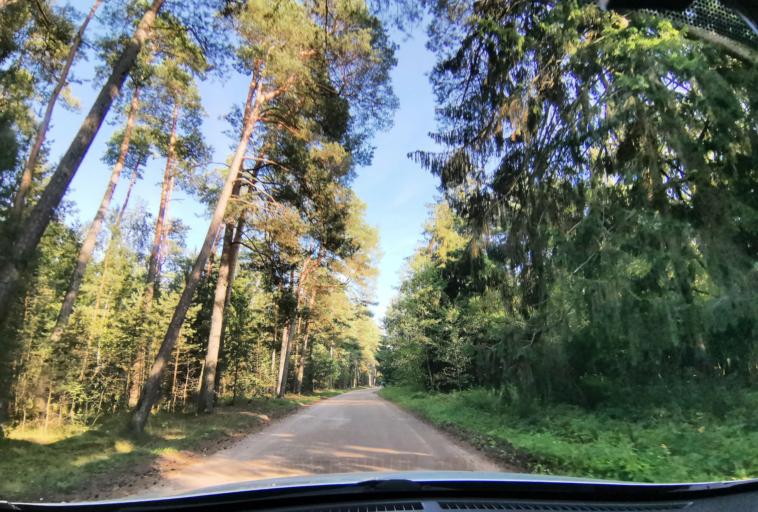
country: LT
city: Nida
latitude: 55.1609
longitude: 20.8321
